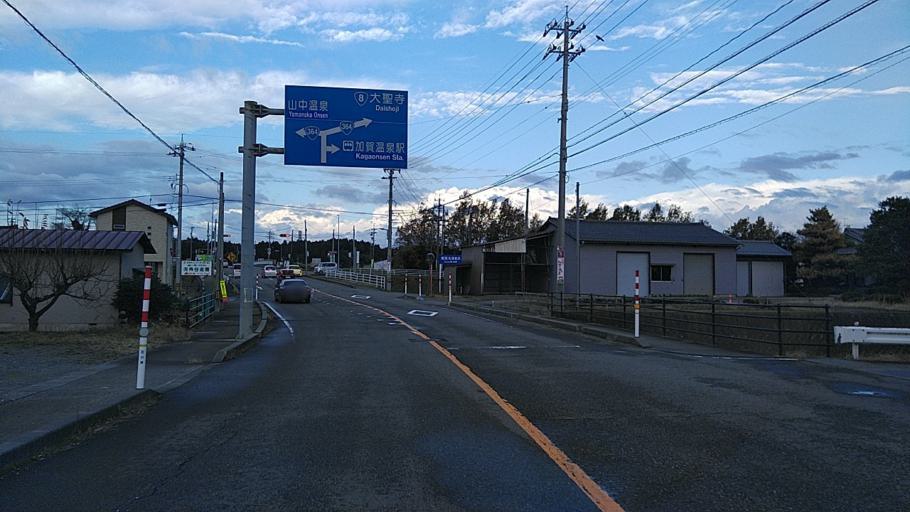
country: JP
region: Ishikawa
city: Komatsu
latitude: 36.2955
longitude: 136.3489
